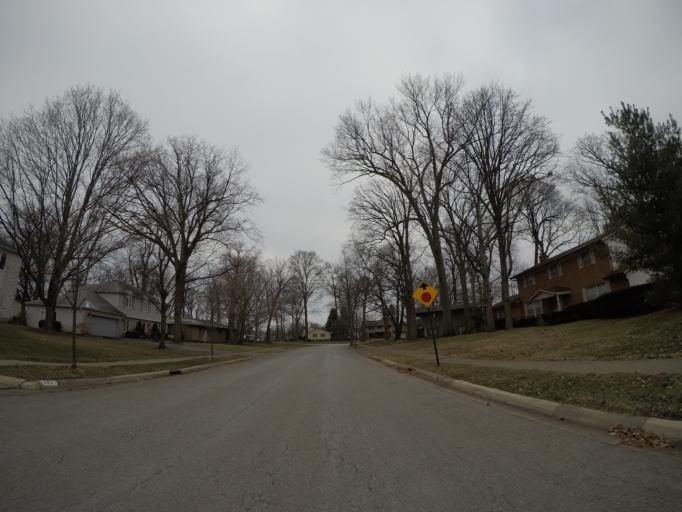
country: US
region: Ohio
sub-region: Franklin County
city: Upper Arlington
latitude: 40.0481
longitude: -83.0588
